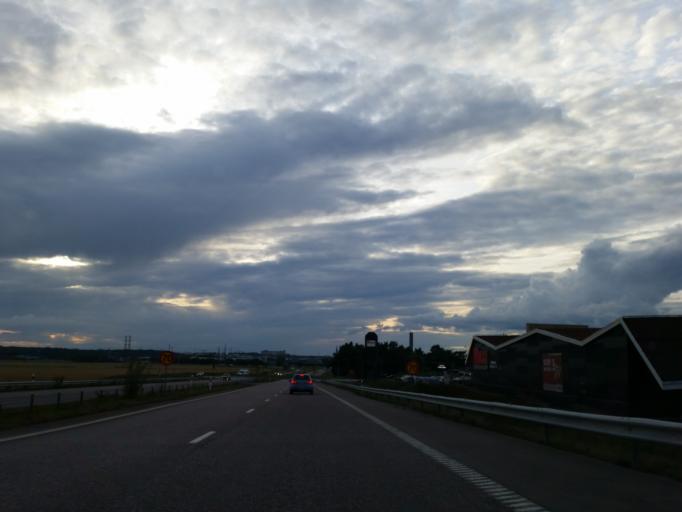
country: SE
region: Uppsala
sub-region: Uppsala Kommun
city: Saevja
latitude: 59.8422
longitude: 17.7152
